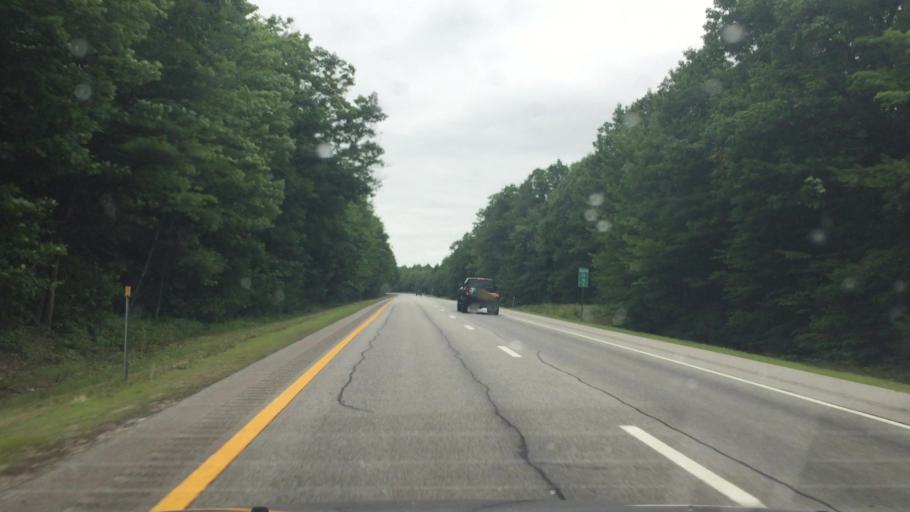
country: US
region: New Hampshire
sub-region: Belknap County
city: Sanbornton
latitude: 43.4727
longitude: -71.5839
